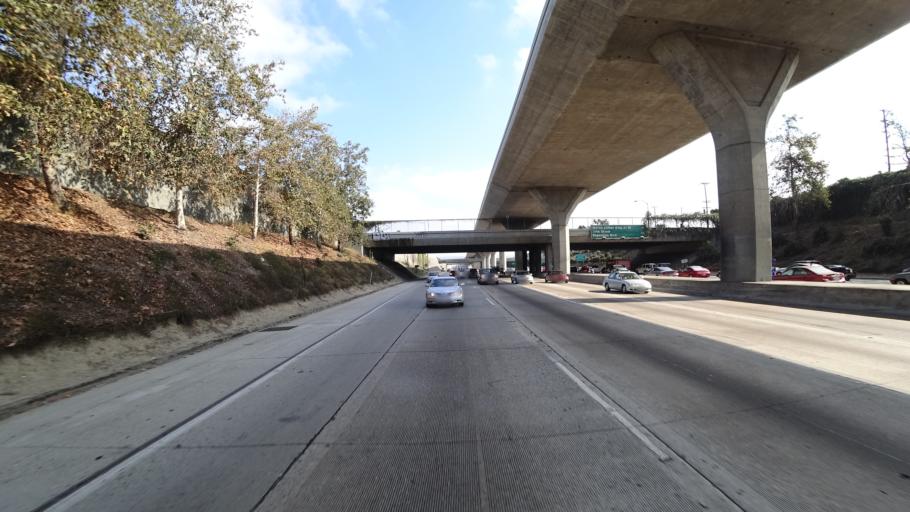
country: US
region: California
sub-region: Los Angeles County
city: Florence-Graham
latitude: 34.0032
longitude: -118.2813
